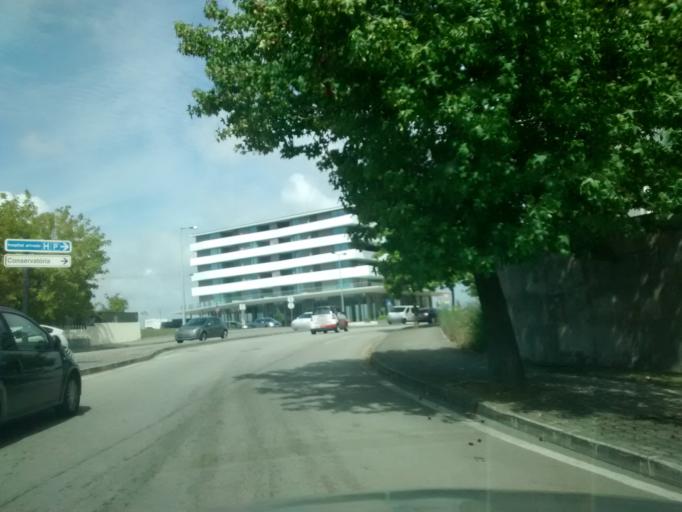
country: PT
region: Aveiro
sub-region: Aveiro
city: Aveiro
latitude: 40.6405
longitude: -8.6402
